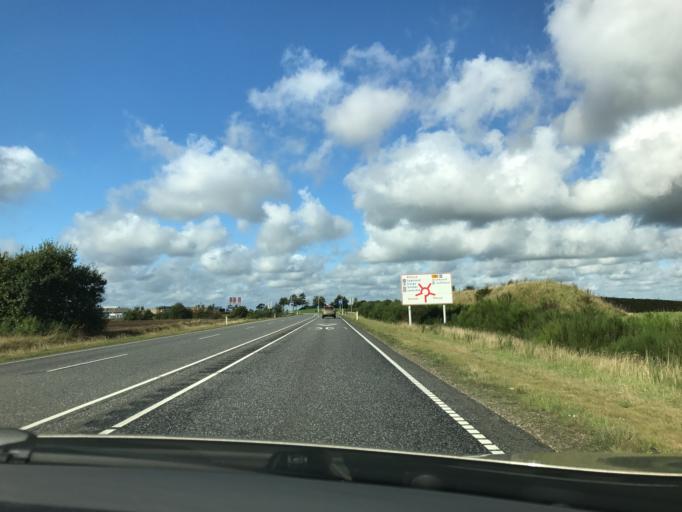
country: DK
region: South Denmark
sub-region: Billund Kommune
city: Billund
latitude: 55.7127
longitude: 9.2228
